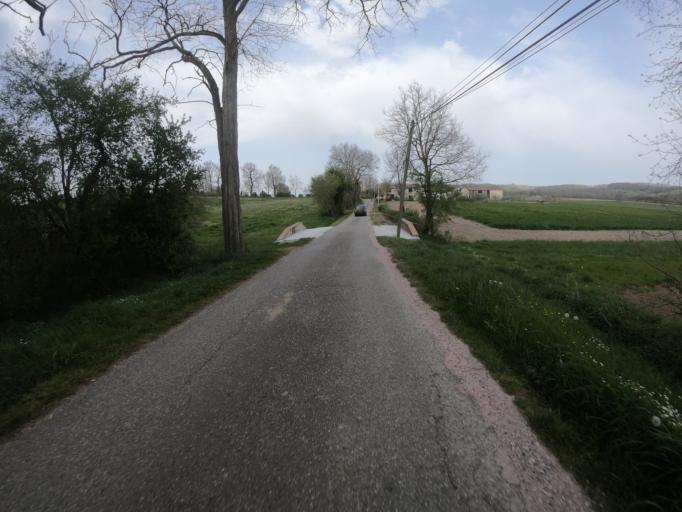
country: FR
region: Languedoc-Roussillon
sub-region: Departement de l'Aude
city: Belpech
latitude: 43.1516
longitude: 1.7155
